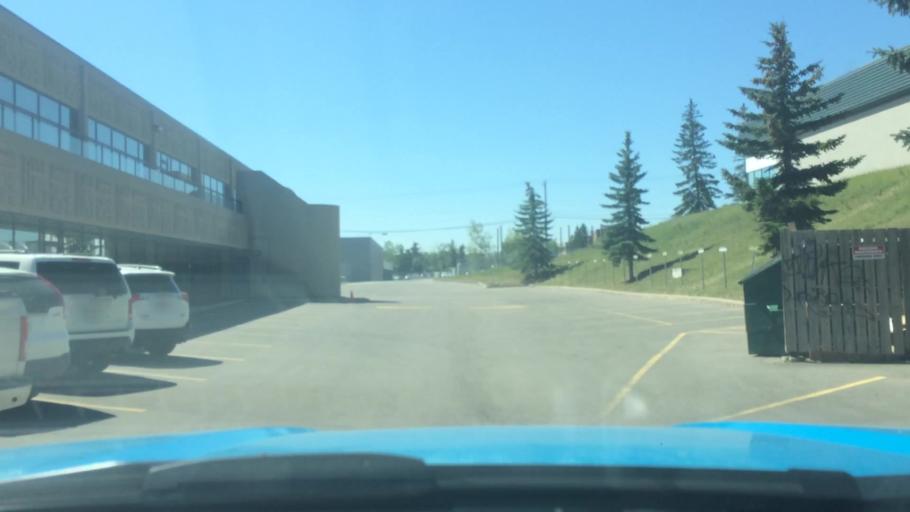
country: CA
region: Alberta
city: Calgary
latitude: 51.0555
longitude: -113.9909
